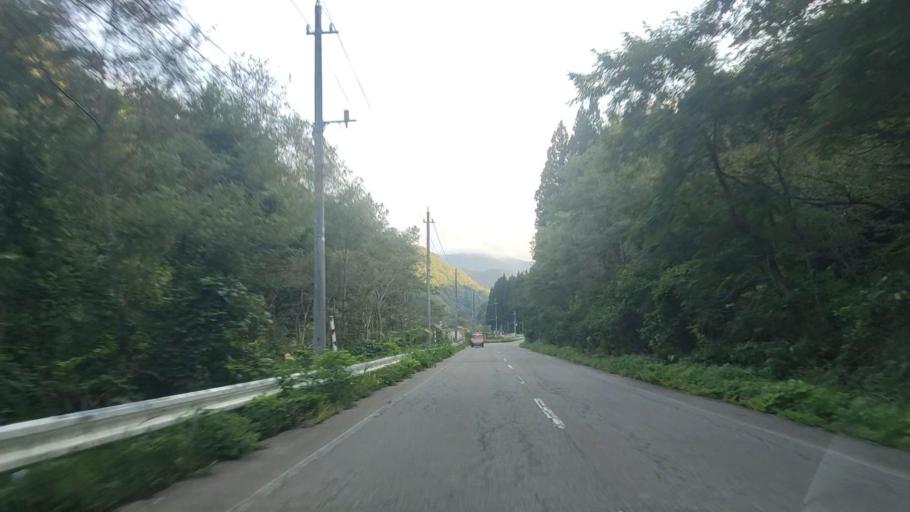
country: JP
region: Toyama
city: Yatsuomachi-higashikumisaka
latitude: 36.4823
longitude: 137.0481
